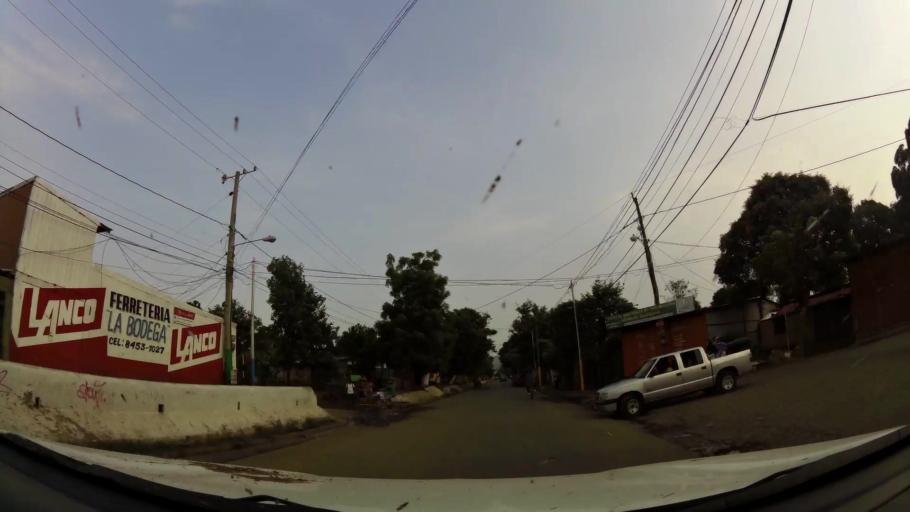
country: NI
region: Masaya
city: Masaya
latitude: 11.9824
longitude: -86.1023
